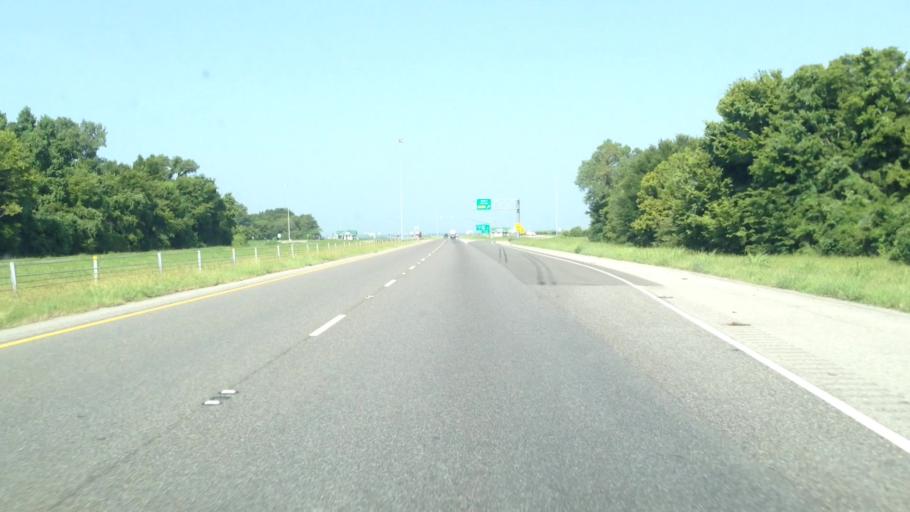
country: US
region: Mississippi
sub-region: Warren County
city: Vicksburg
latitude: 32.3208
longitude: -90.9425
